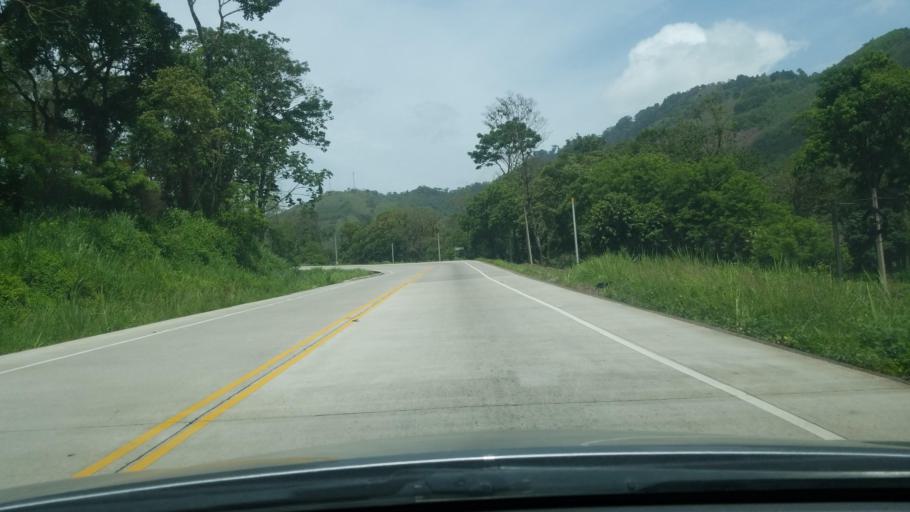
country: HN
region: Copan
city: Agua Caliente
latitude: 14.8712
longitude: -88.7830
